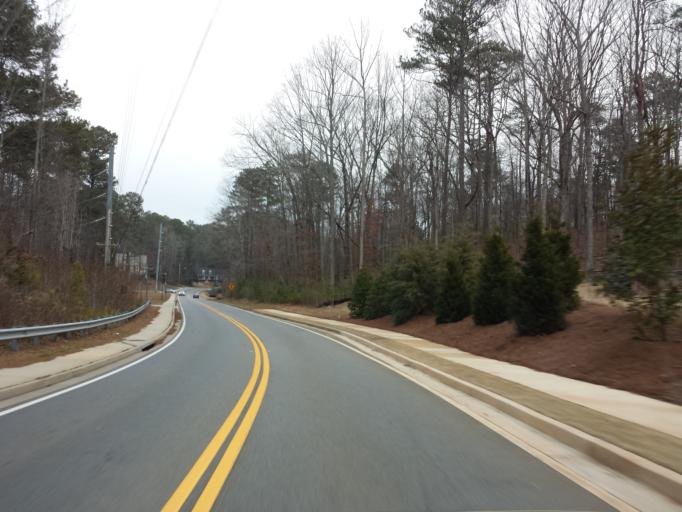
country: US
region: Georgia
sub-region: Fulton County
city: Roswell
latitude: 34.0184
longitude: -84.4127
